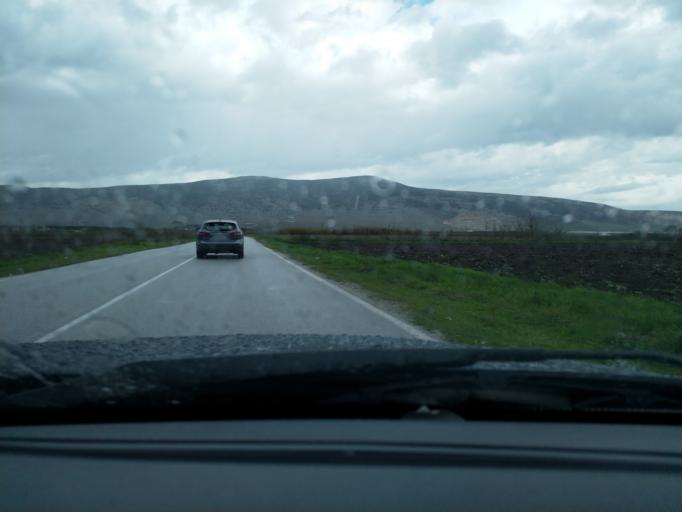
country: GR
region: Thessaly
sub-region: Trikala
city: Taxiarches
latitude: 39.5527
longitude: 21.8896
